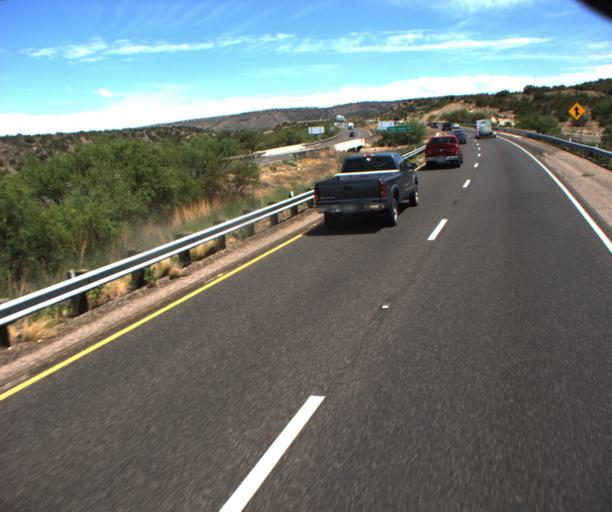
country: US
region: Arizona
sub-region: Yavapai County
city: Lake Montezuma
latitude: 34.6893
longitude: -111.7434
